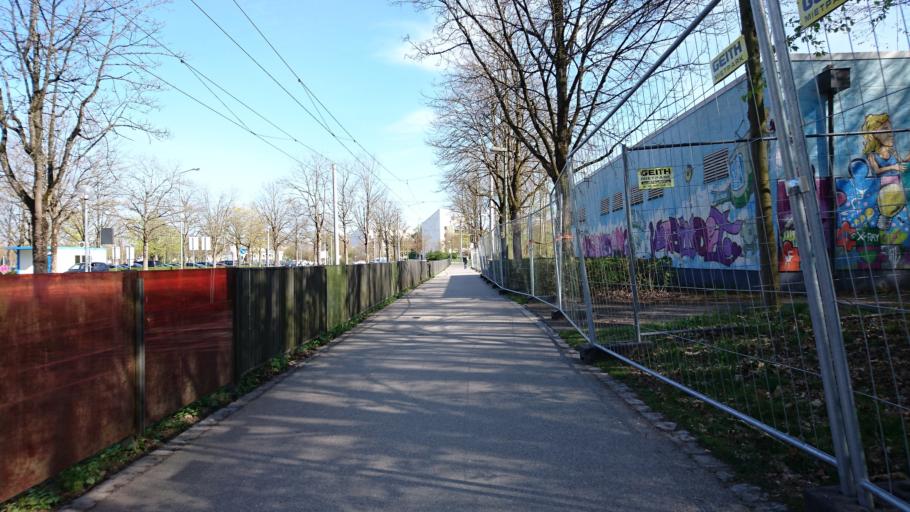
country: DE
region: Bavaria
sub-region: Swabia
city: Stadtbergen
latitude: 48.3829
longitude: 10.8393
